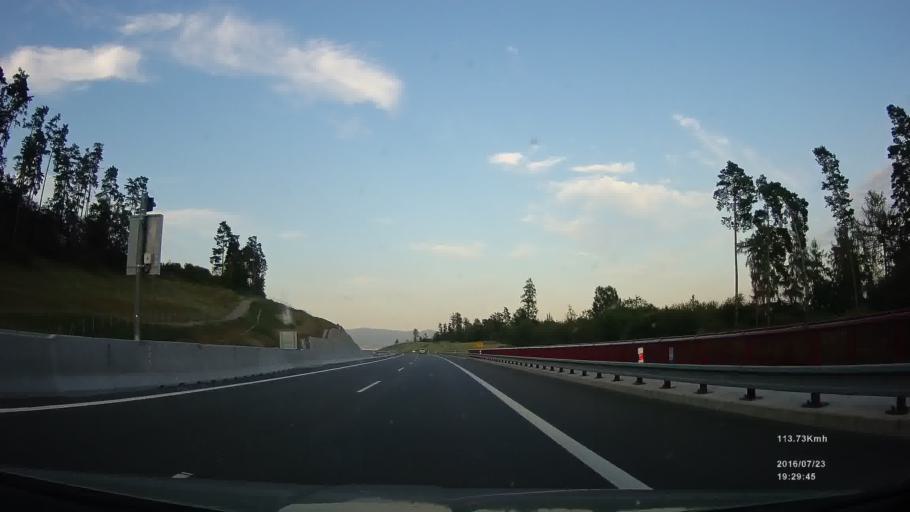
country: SK
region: Presovsky
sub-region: Okres Presov
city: Levoca
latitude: 49.0061
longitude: 20.6387
